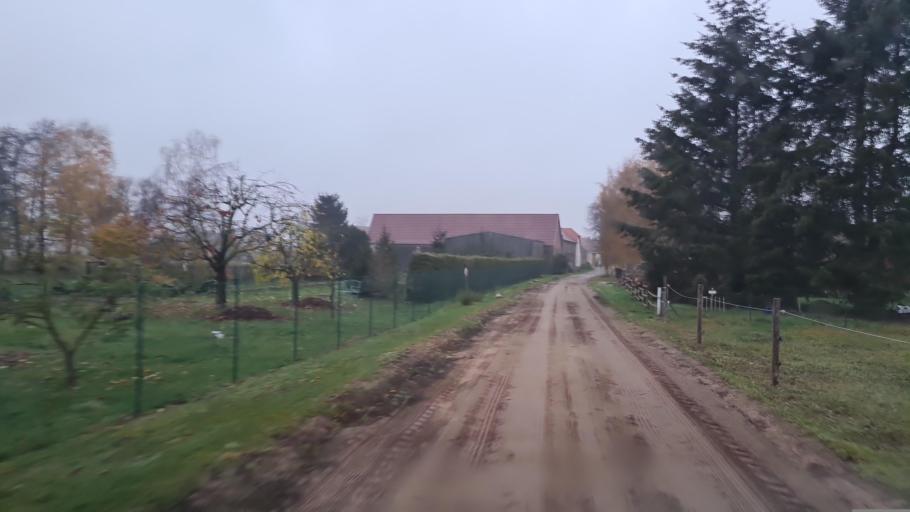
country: DE
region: Brandenburg
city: Beelitz
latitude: 52.2419
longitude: 13.0228
